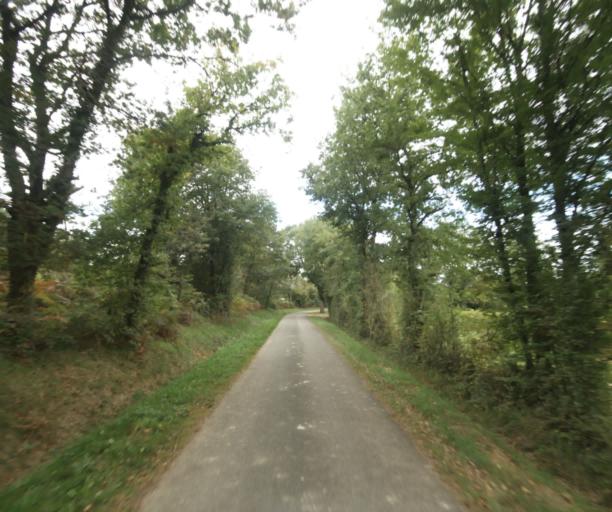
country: FR
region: Midi-Pyrenees
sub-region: Departement du Gers
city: Eauze
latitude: 43.9076
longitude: 0.1190
